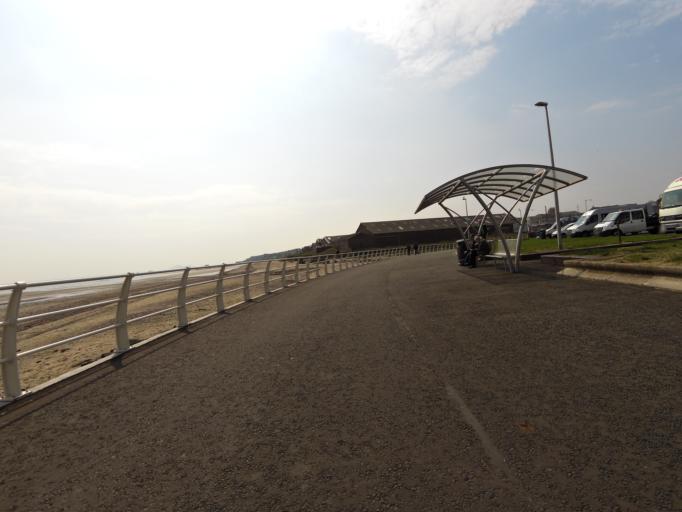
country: GB
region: Scotland
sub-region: Fife
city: Kirkcaldy
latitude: 56.0999
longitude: -3.1598
